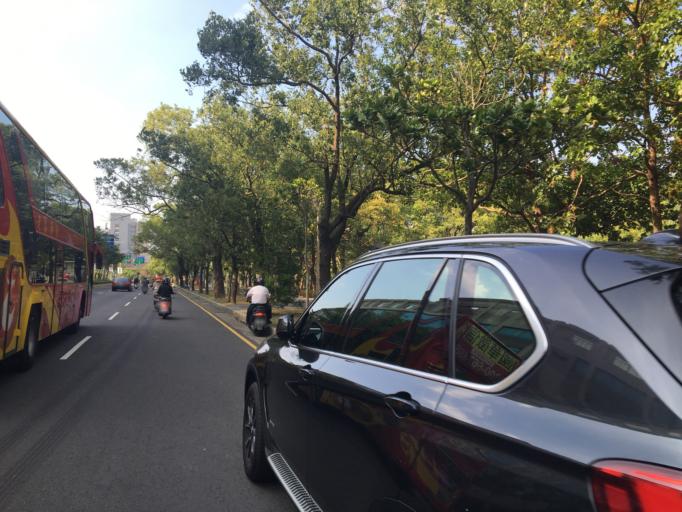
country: TW
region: Taiwan
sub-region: Hsinchu
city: Hsinchu
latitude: 24.7978
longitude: 120.9955
